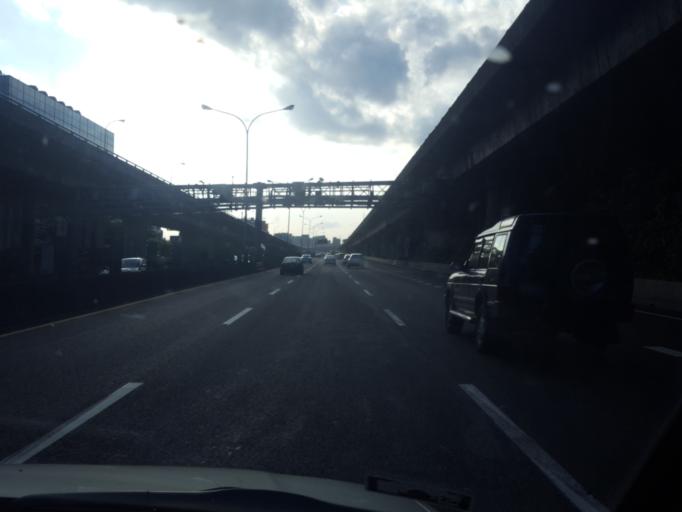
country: TW
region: Taipei
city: Taipei
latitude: 25.0648
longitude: 121.6066
